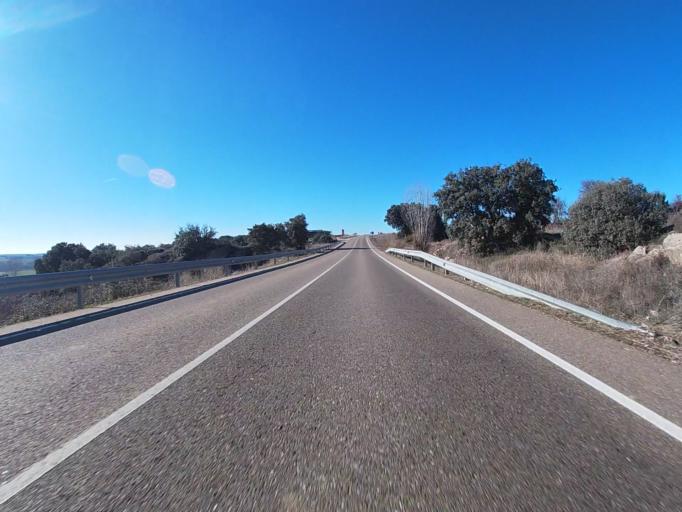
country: ES
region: Castille and Leon
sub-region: Provincia de Salamanca
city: Juzbado
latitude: 41.0780
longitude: -5.8522
